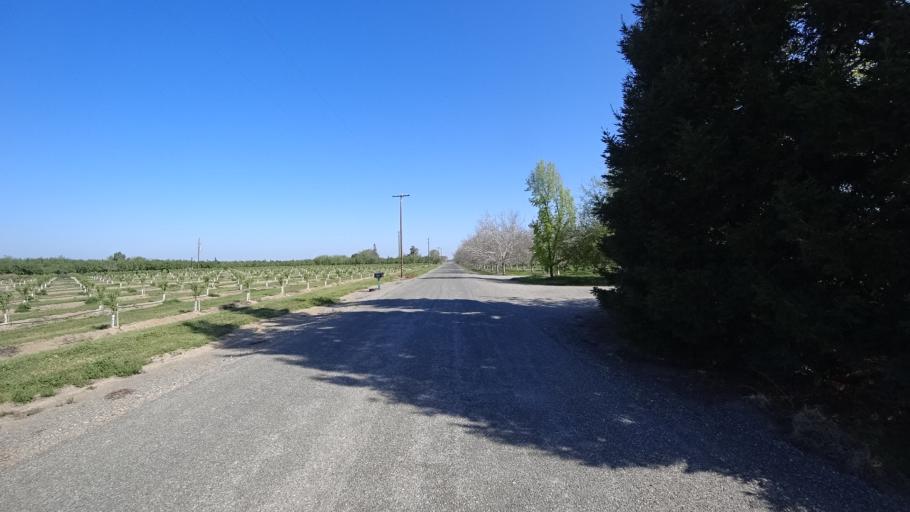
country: US
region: California
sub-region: Glenn County
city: Hamilton City
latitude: 39.6198
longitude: -122.0275
